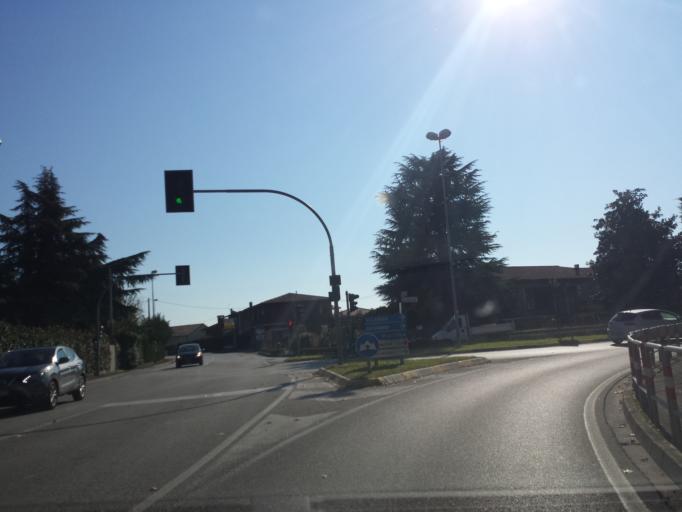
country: IT
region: Veneto
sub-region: Provincia di Vicenza
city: Camisano Vicentino
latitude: 45.5223
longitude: 11.7184
